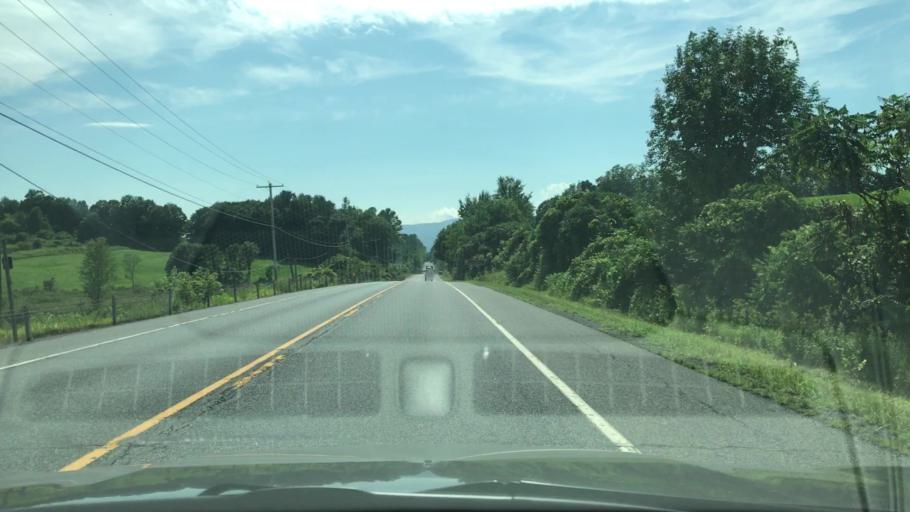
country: US
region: Vermont
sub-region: Rutland County
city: Fair Haven
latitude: 43.5704
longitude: -73.3173
